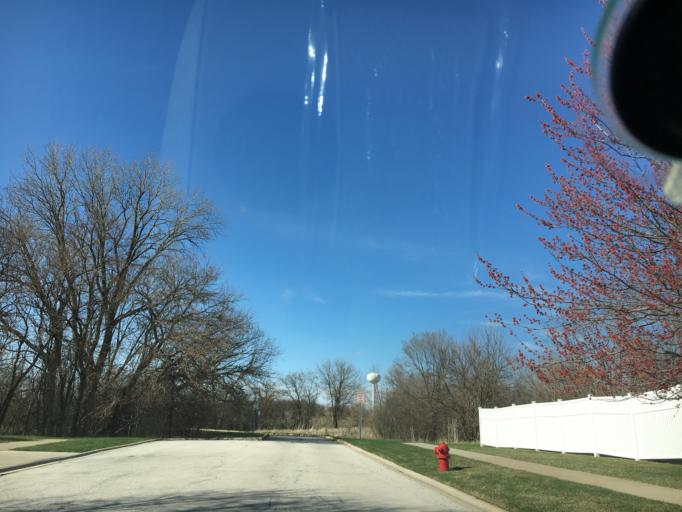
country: US
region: Illinois
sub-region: Cook County
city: Oak Forest
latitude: 41.5913
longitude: -87.7345
